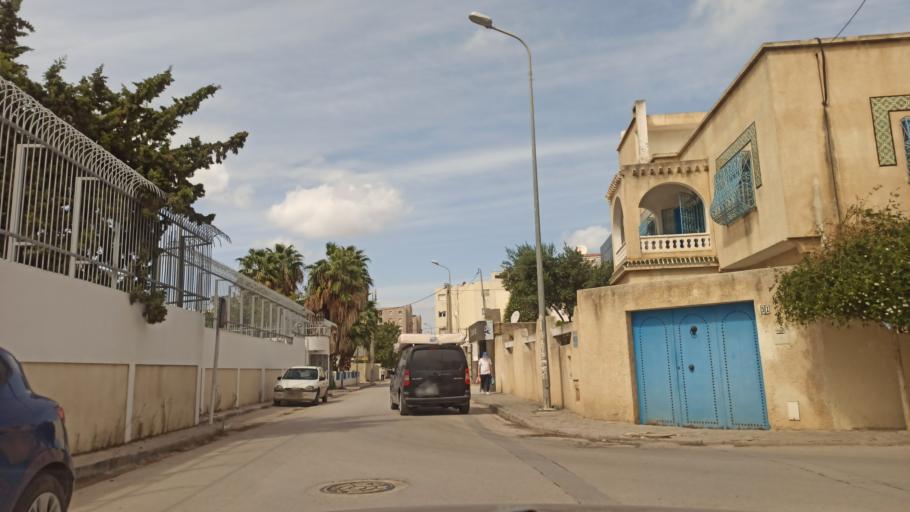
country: TN
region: Tunis
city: La Goulette
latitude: 36.8540
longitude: 10.2691
